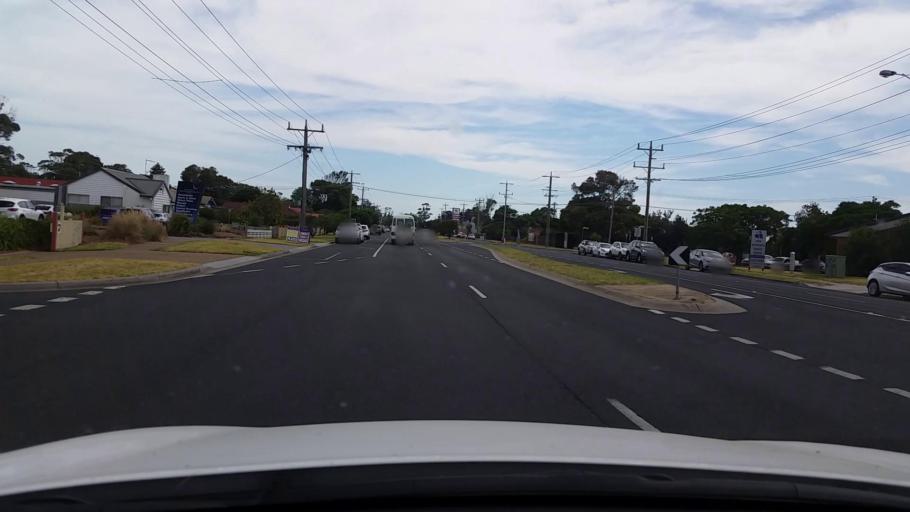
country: AU
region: Victoria
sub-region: Mornington Peninsula
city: Rosebud West
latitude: -38.3645
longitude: 144.8895
